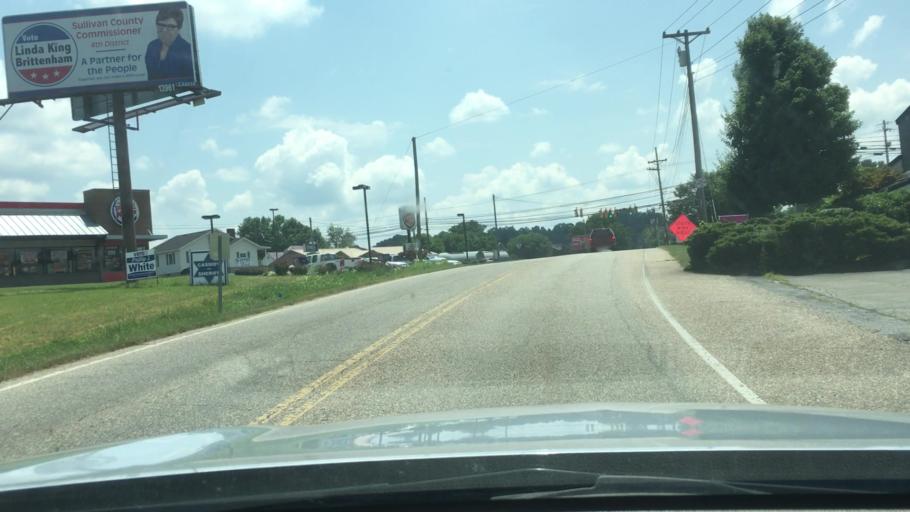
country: US
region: Tennessee
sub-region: Sullivan County
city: Blountville
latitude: 36.5352
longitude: -82.3208
